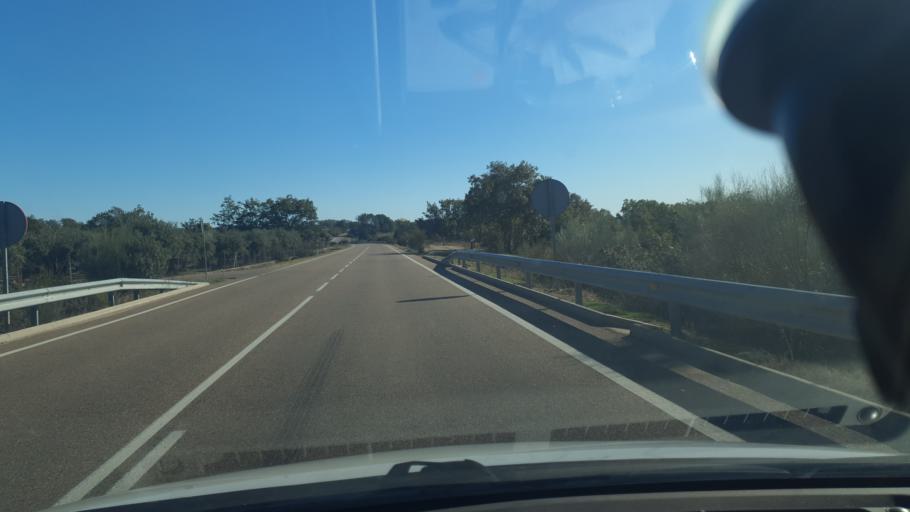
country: ES
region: Castille and Leon
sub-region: Provincia de Avila
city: Candeleda
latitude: 40.1382
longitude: -5.2479
